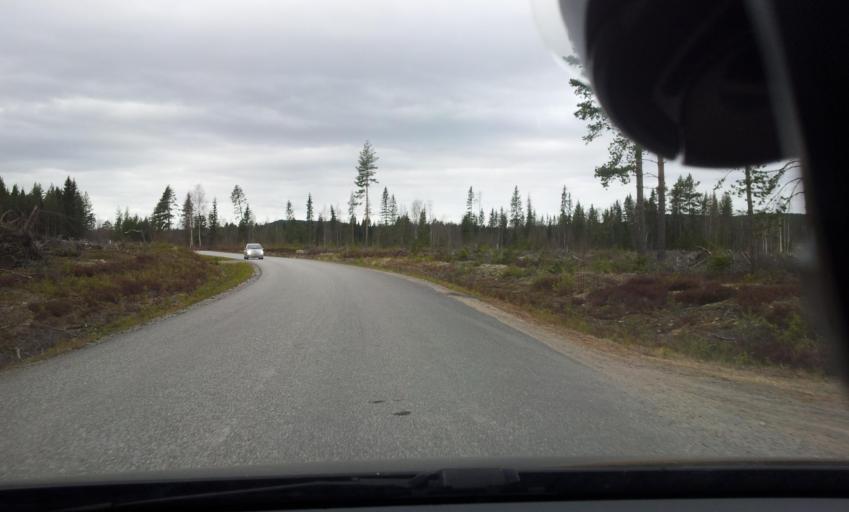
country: SE
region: Gaevleborg
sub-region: Ljusdals Kommun
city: Farila
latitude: 61.8219
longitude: 15.9647
